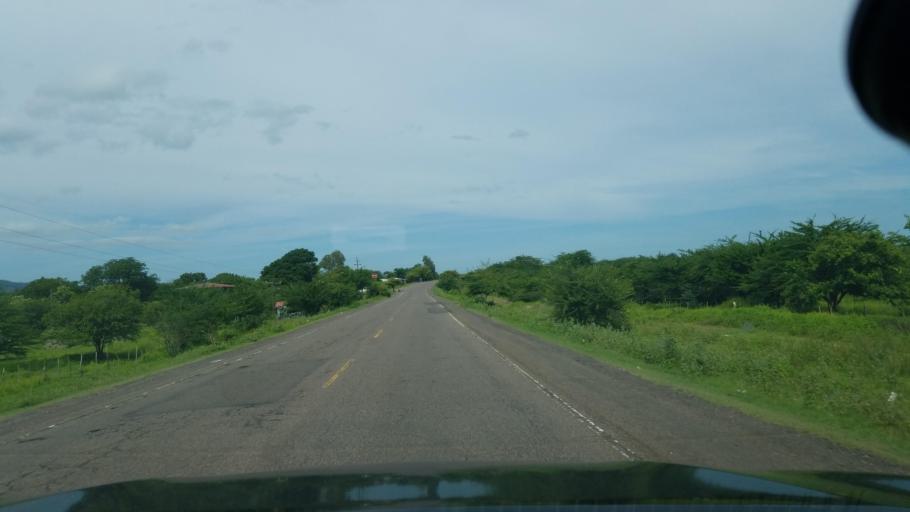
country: HN
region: Choluteca
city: Santa Ana de Yusguare
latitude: 13.3522
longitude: -87.1060
